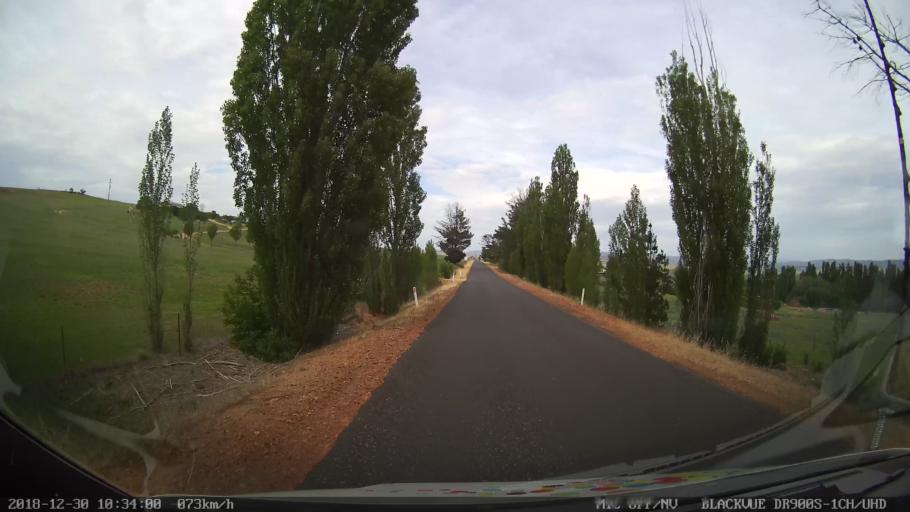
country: AU
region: New South Wales
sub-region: Snowy River
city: Berridale
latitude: -36.4992
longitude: 148.8458
